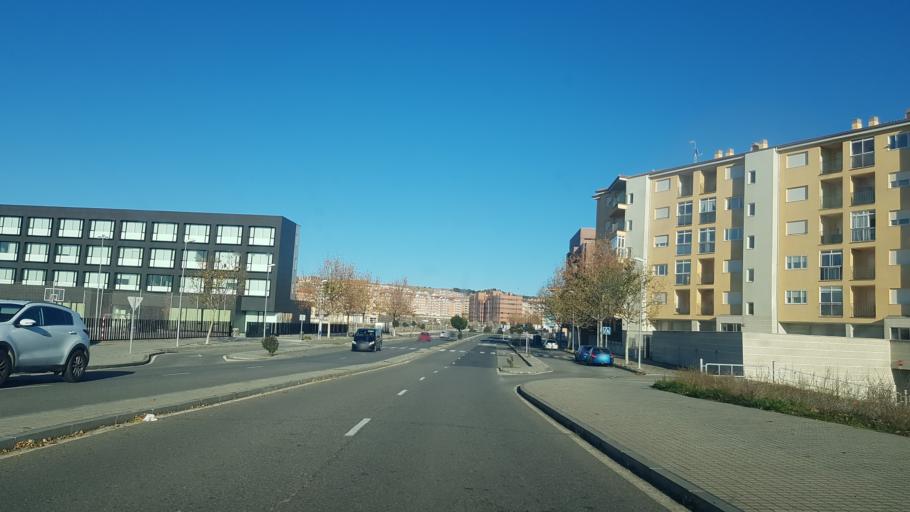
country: ES
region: Castille and Leon
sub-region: Provincia de Avila
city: Avila
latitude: 40.6426
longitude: -4.6868
